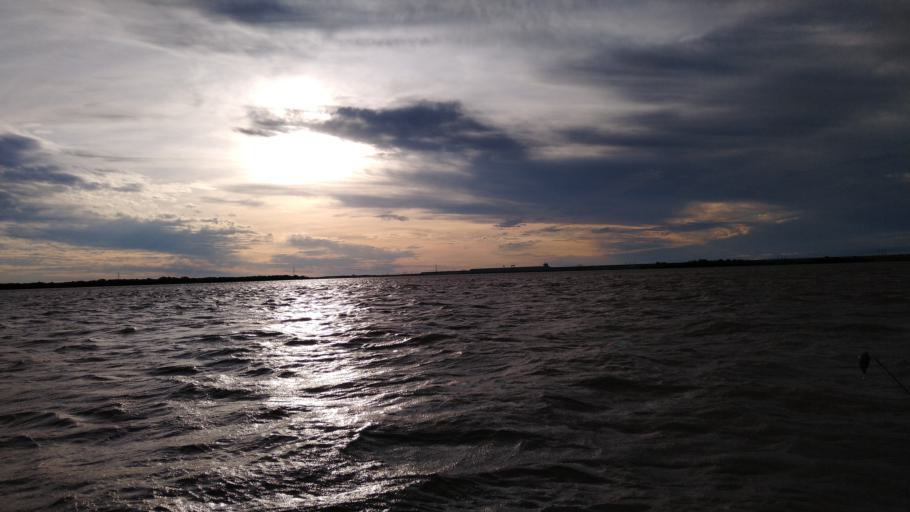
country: AR
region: Corrientes
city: Ituzaingo
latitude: -27.5145
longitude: -56.7019
